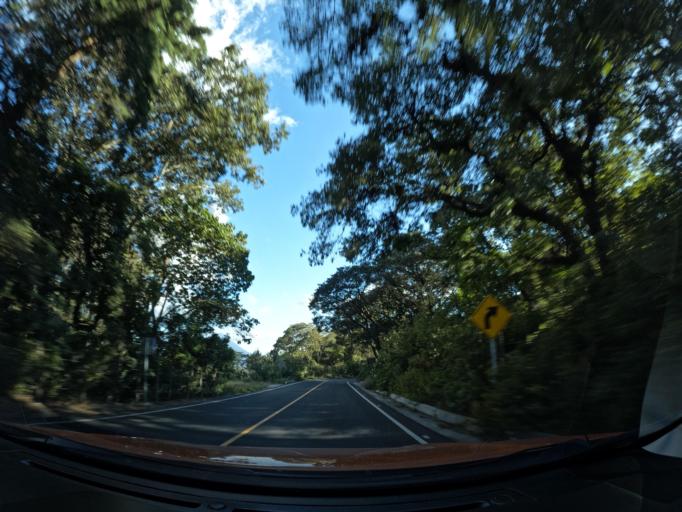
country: GT
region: Escuintla
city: Palin
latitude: 14.4609
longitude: -90.6943
